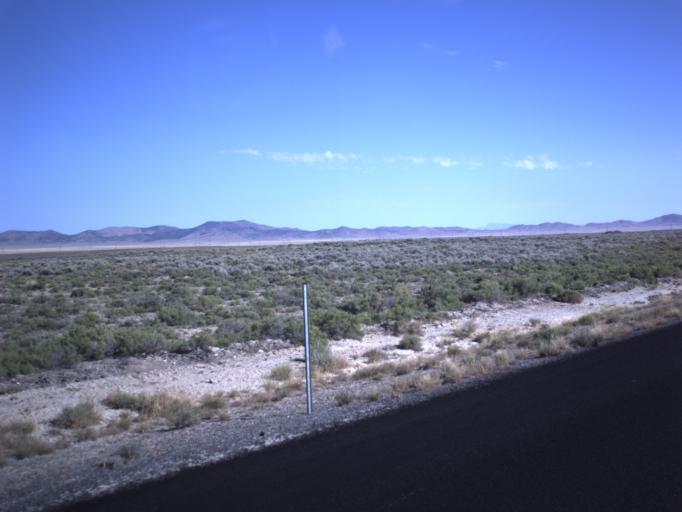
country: US
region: Utah
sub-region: Beaver County
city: Milford
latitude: 38.5340
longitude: -112.9912
